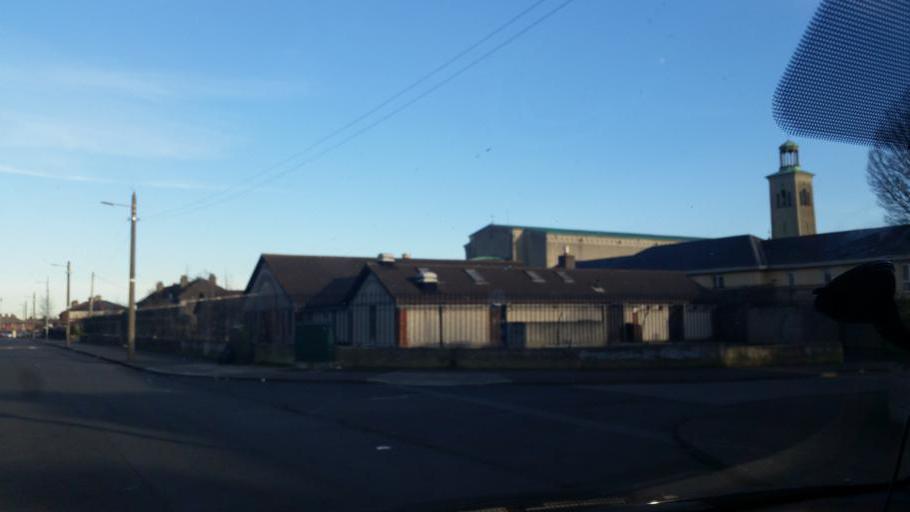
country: IE
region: Leinster
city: Cabra
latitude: 53.3687
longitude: -6.2969
